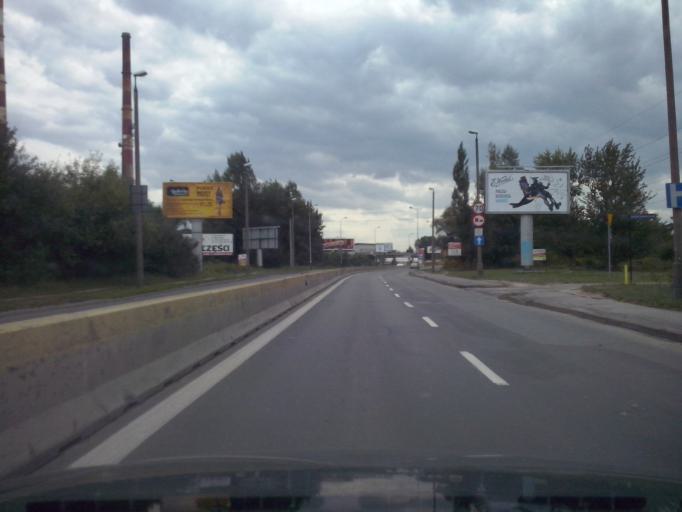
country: PL
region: Lesser Poland Voivodeship
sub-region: Krakow
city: Krakow
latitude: 50.0600
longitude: 20.0033
